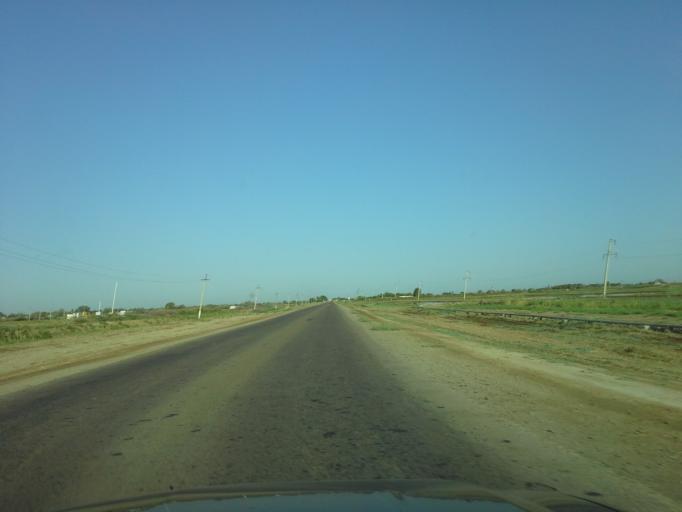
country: UZ
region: Karakalpakstan
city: Khujayli
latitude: 42.2257
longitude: 59.4770
